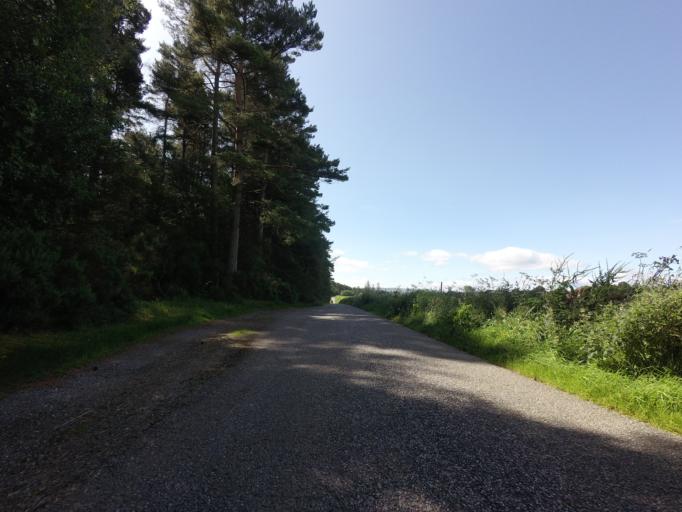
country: GB
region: Scotland
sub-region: Highland
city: Nairn
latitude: 57.5233
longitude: -3.8647
